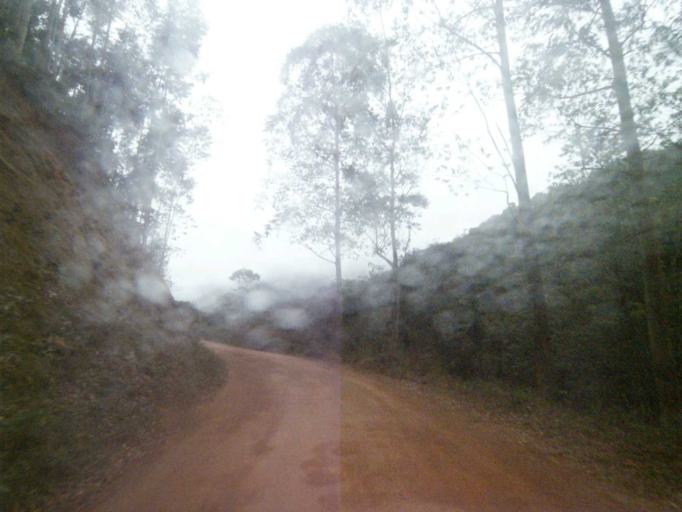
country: BR
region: Santa Catarina
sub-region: Anitapolis
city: Anitapolis
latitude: -27.8865
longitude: -49.1330
